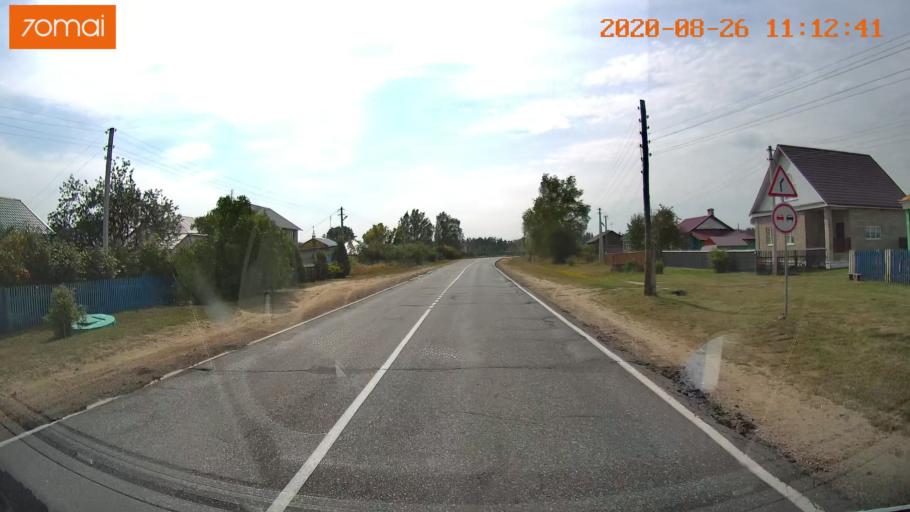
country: RU
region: Rjazan
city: Izhevskoye
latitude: 54.4677
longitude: 41.1247
